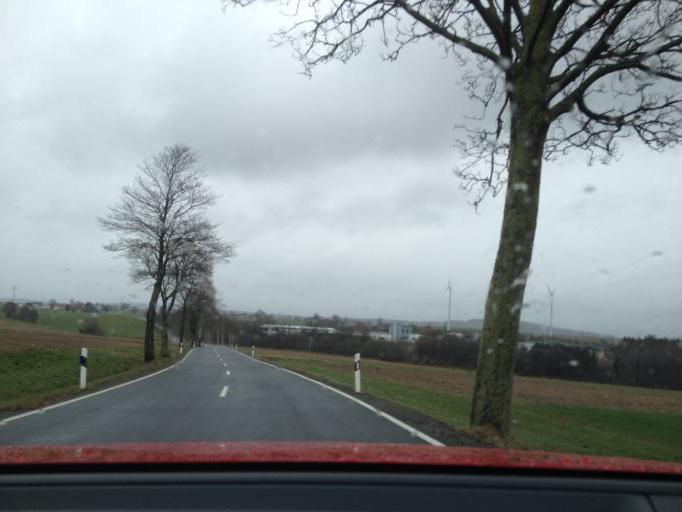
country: DE
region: Bavaria
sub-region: Upper Franconia
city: Arzberg
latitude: 50.0781
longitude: 12.1636
